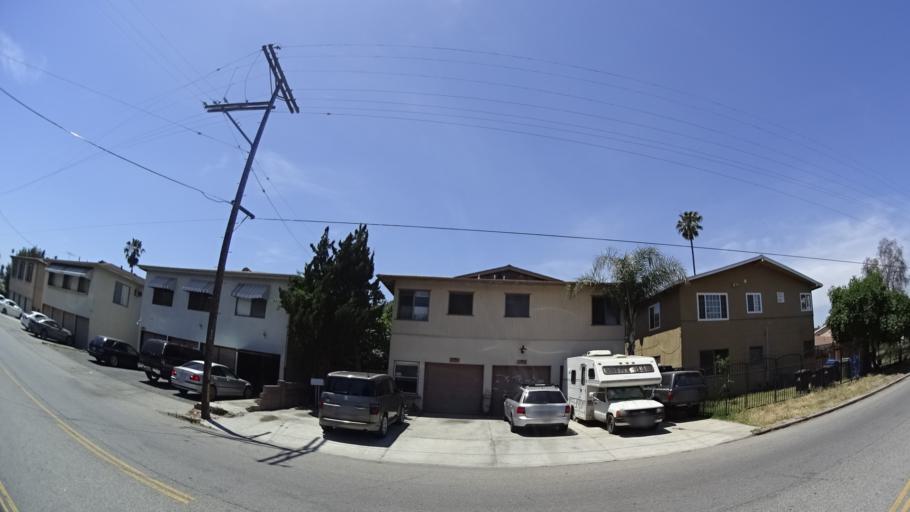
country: US
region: California
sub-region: Los Angeles County
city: North Hollywood
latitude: 34.1817
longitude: -118.3790
